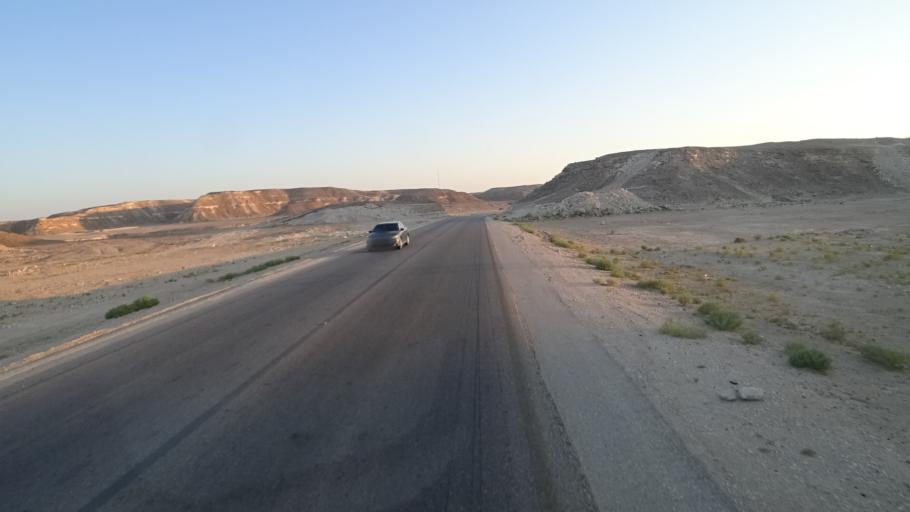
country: OM
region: Zufar
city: Salalah
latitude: 17.4979
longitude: 53.3623
